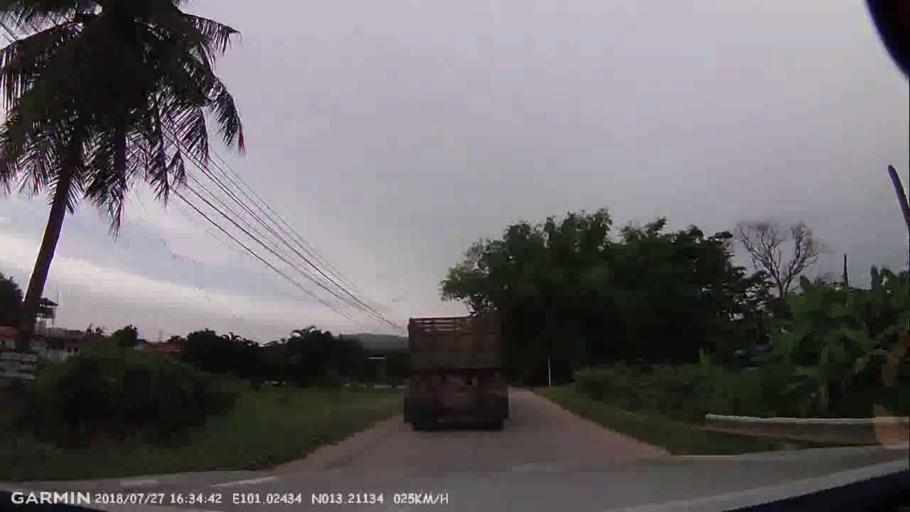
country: TH
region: Chon Buri
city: Si Racha
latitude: 13.2114
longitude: 101.0244
